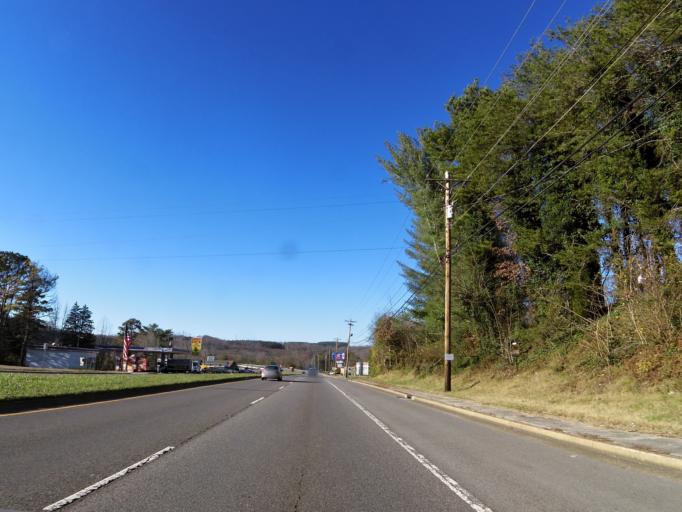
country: US
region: Tennessee
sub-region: Anderson County
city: Oak Ridge
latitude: 35.9873
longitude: -84.1876
